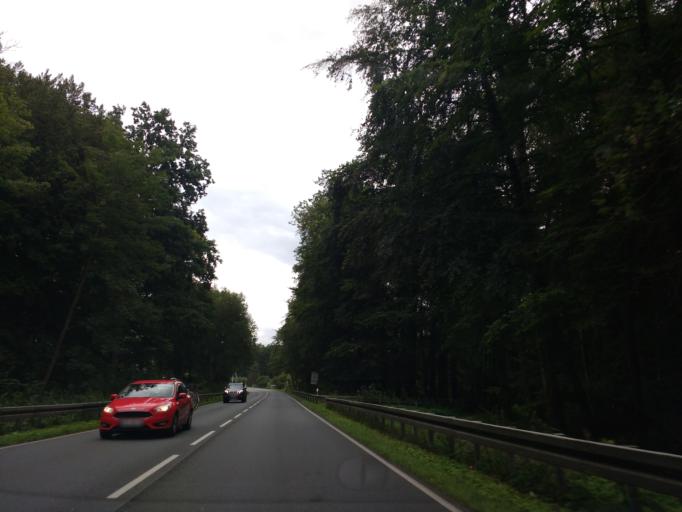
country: DE
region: Lower Saxony
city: Bad Rothenfelde
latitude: 52.1026
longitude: 8.1545
